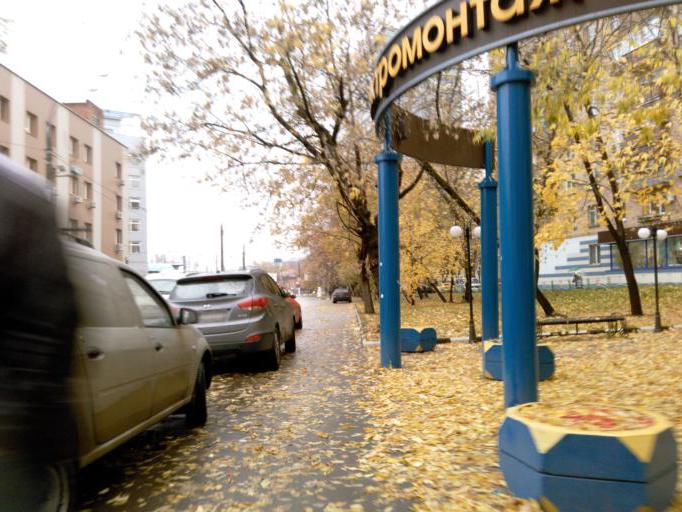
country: RU
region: Moscow
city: Zamoskvorech'ye
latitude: 55.7068
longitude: 37.6177
